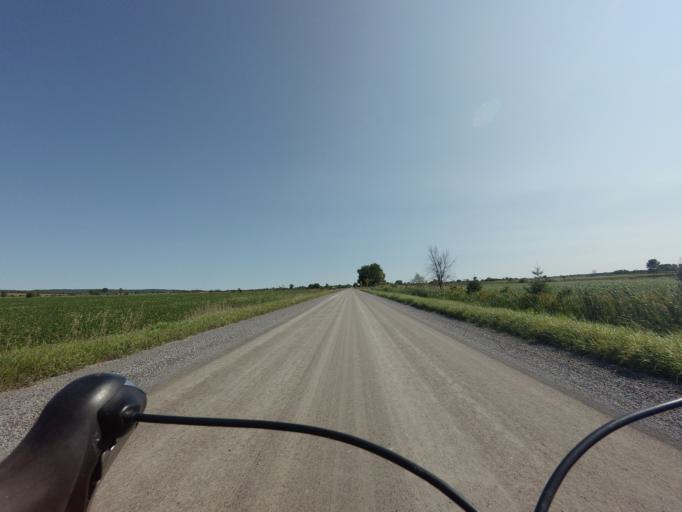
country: CA
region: Ontario
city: Arnprior
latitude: 45.3760
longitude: -76.1452
